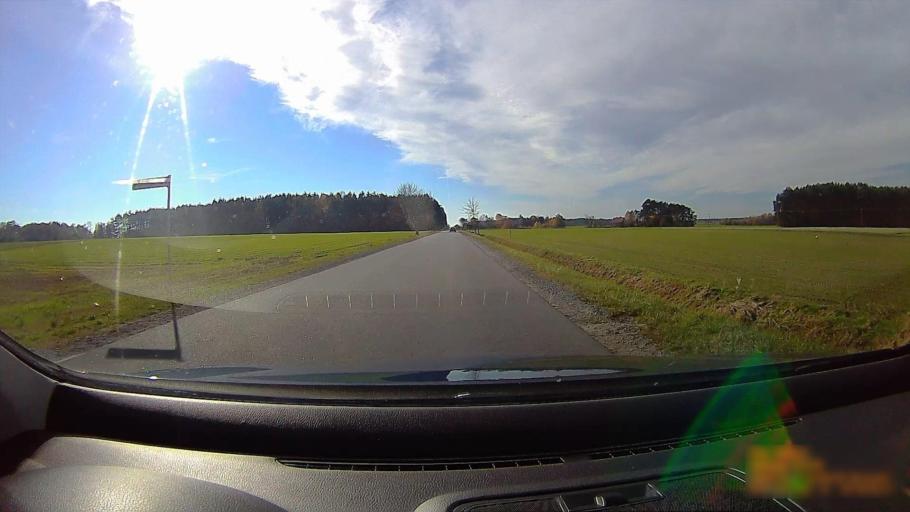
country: PL
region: Greater Poland Voivodeship
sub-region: Powiat ostrzeszowski
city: Doruchow
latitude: 51.3768
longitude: 18.0401
